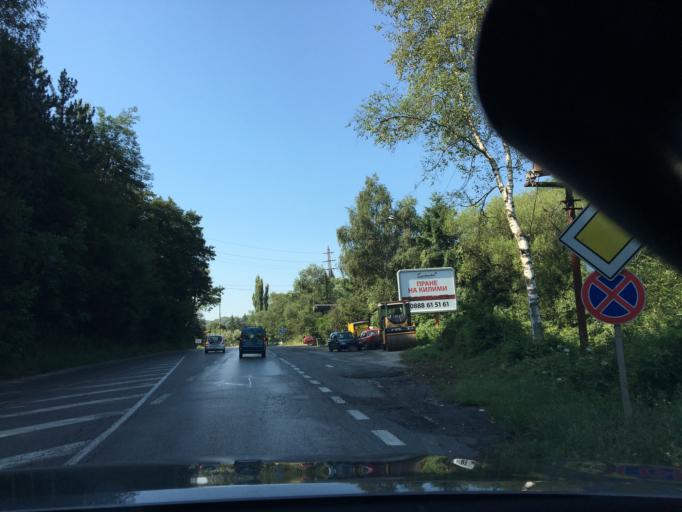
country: BG
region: Sofiya
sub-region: Obshtina Bozhurishte
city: Bozhurishte
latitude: 42.6367
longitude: 23.1961
